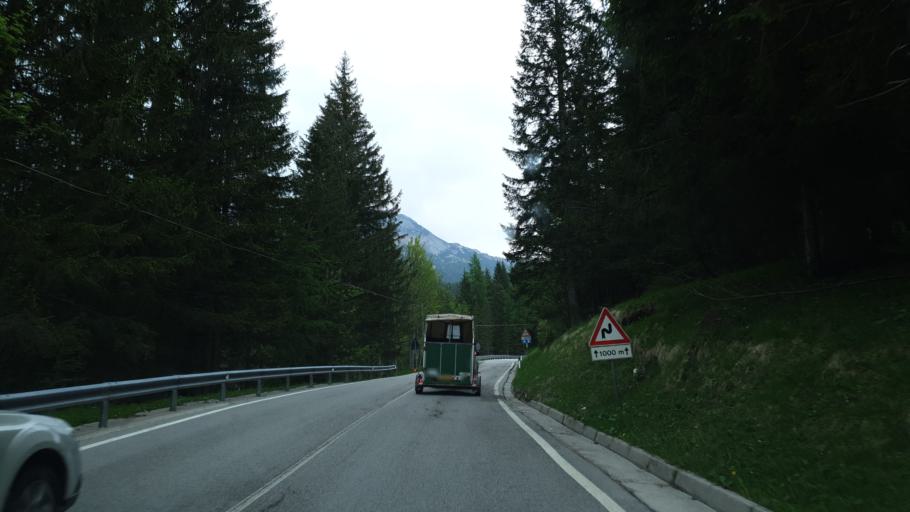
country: IT
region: Veneto
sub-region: Provincia di Belluno
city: San Vito
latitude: 46.5542
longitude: 12.2457
